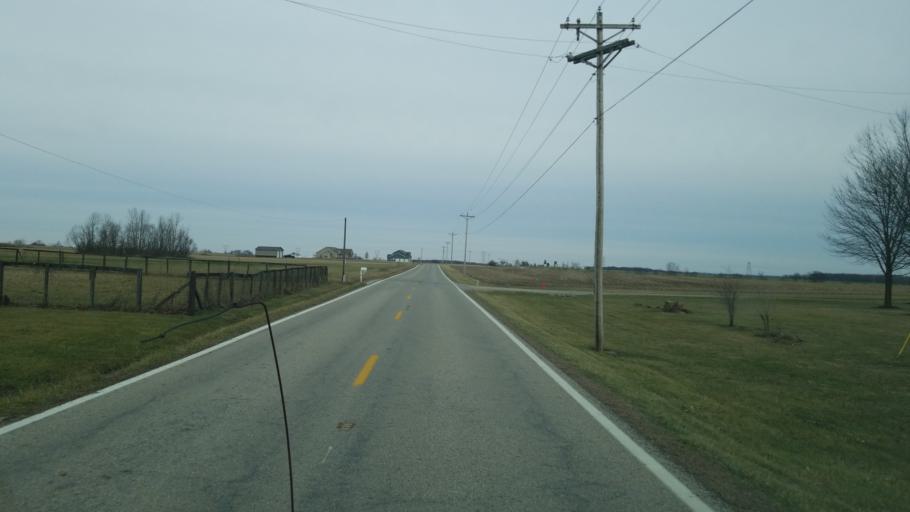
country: US
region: Ohio
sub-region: Pickaway County
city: Williamsport
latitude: 39.5145
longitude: -83.1454
